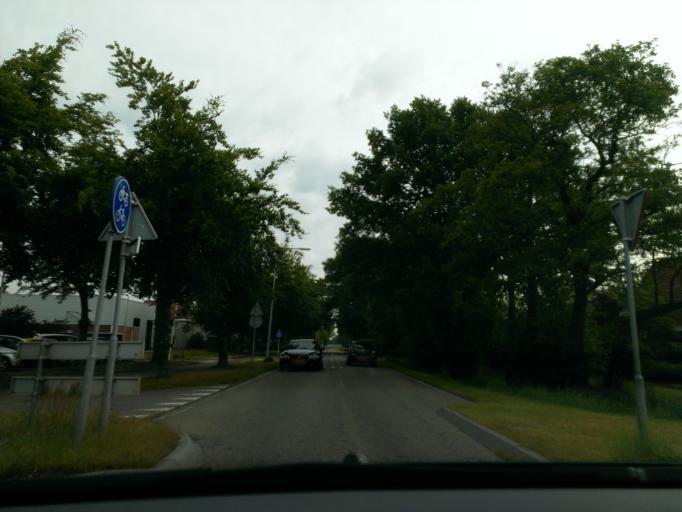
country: NL
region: Overijssel
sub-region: Gemeente Almelo
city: Almelo
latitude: 52.3320
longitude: 6.6561
